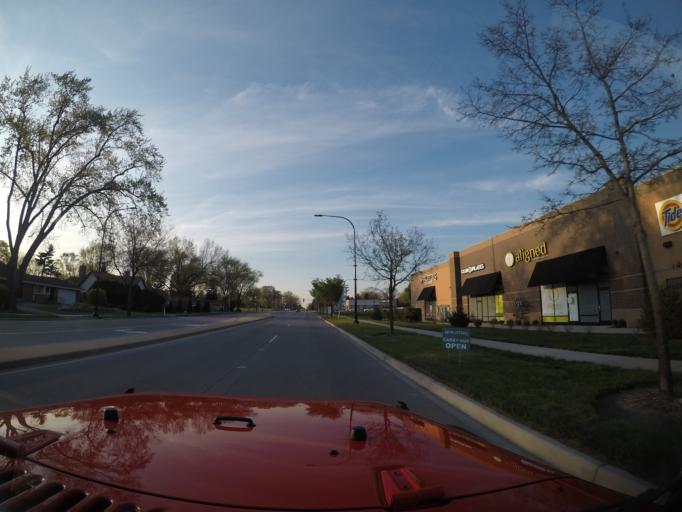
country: US
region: Illinois
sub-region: Cook County
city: Prospect Heights
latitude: 42.0867
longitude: -87.9368
